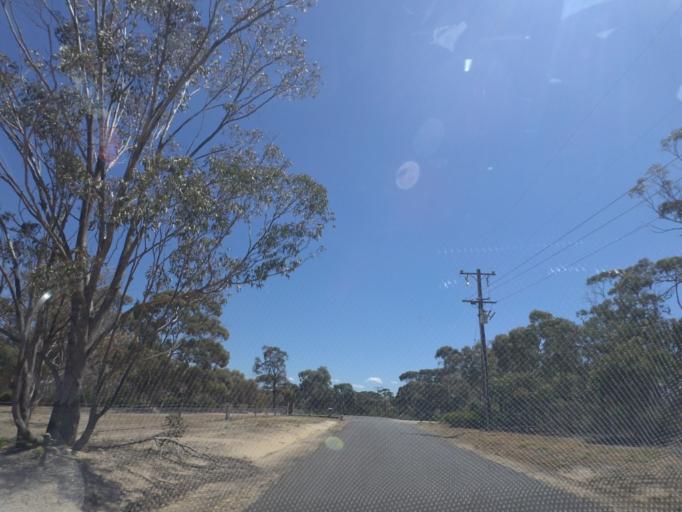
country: AU
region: Victoria
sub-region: Moorabool
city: Bacchus Marsh
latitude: -37.6433
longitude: 144.5045
